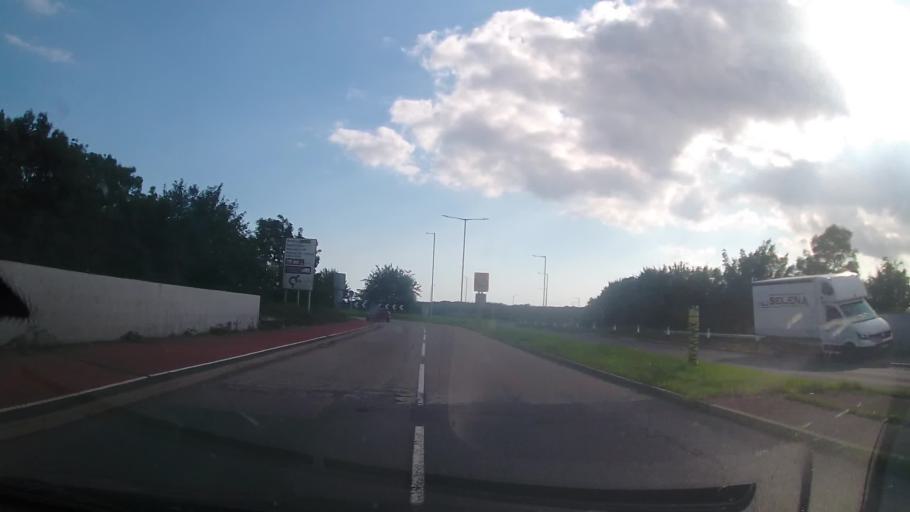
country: GB
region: England
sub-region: Kent
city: Hythe
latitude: 51.0933
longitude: 1.0500
